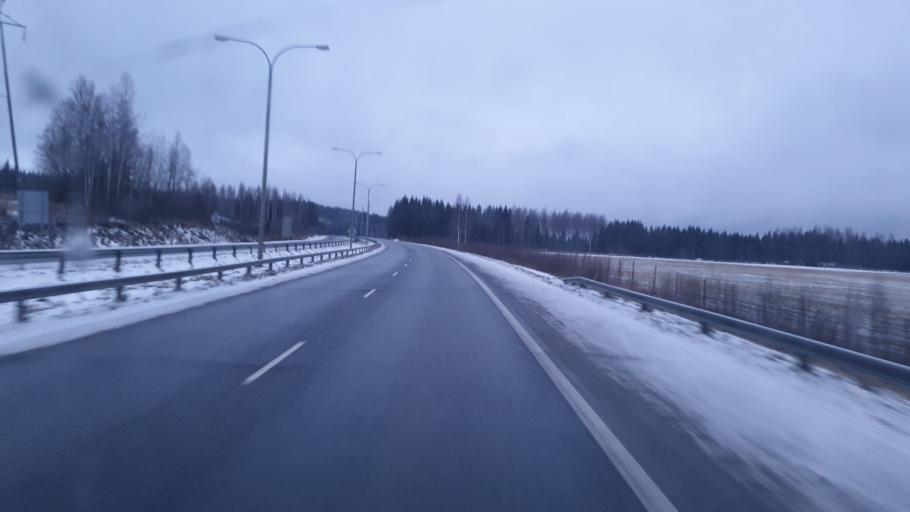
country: FI
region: Northern Savo
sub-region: Kuopio
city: Siilinjaervi
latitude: 63.0476
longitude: 27.6638
